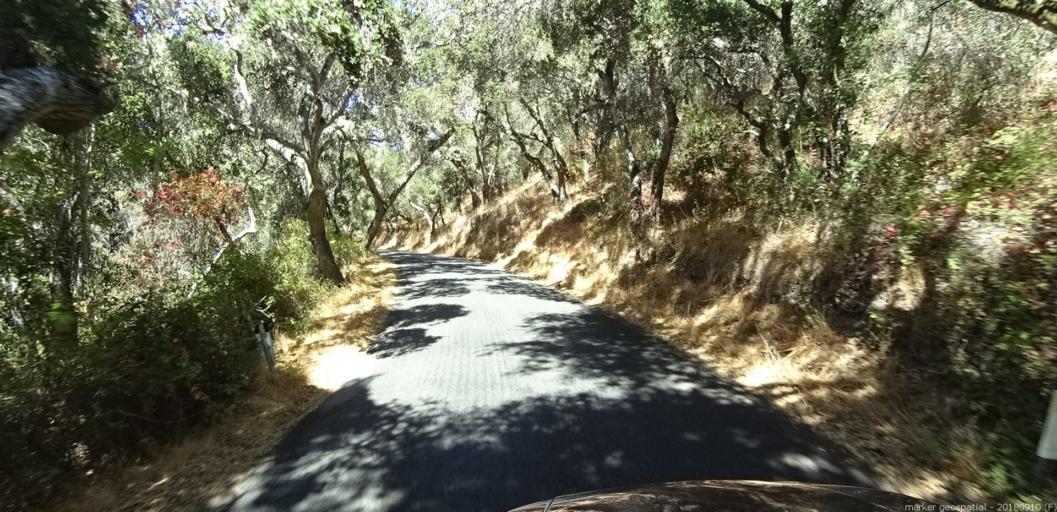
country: US
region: California
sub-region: Monterey County
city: Carmel Valley Village
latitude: 36.4900
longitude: -121.8108
